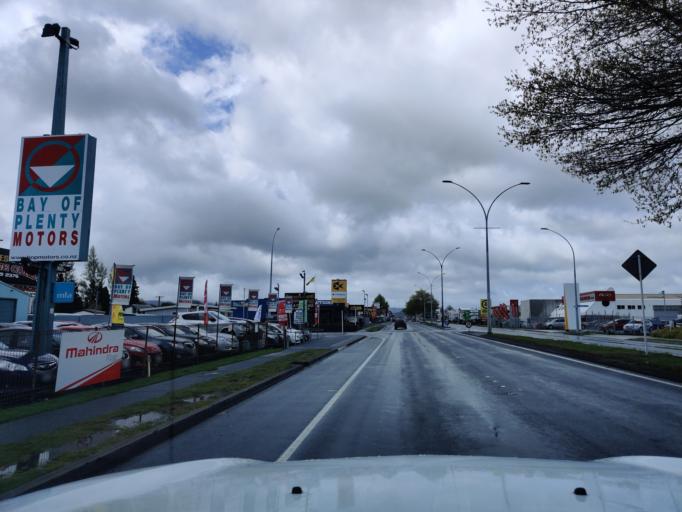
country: NZ
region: Bay of Plenty
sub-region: Rotorua District
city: Rotorua
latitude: -38.1200
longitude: 176.2287
